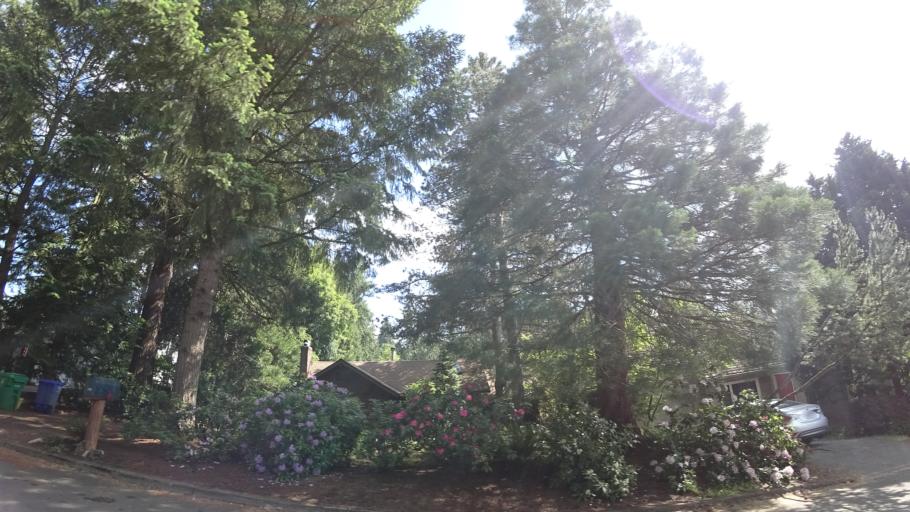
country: US
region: Oregon
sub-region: Washington County
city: Garden Home-Whitford
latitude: 45.4716
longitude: -122.7160
